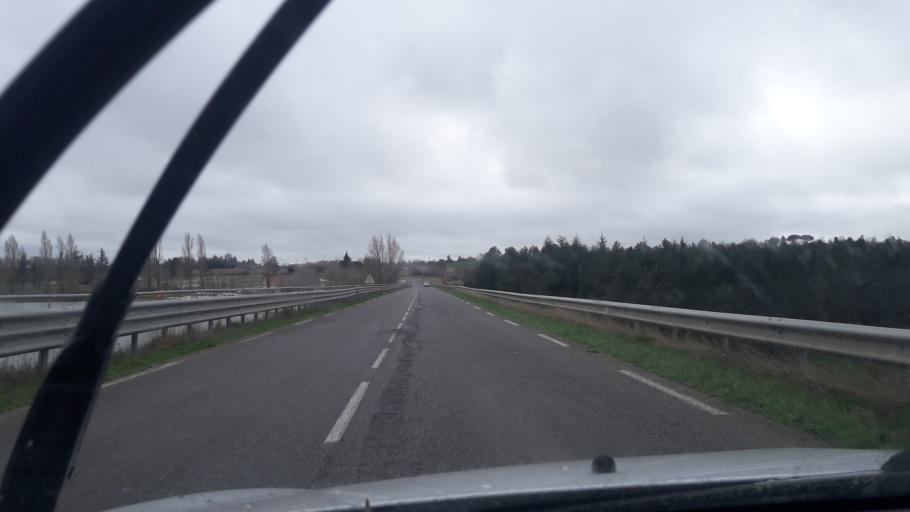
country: FR
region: Midi-Pyrenees
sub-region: Departement du Gers
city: Gimont
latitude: 43.6908
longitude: 0.9984
